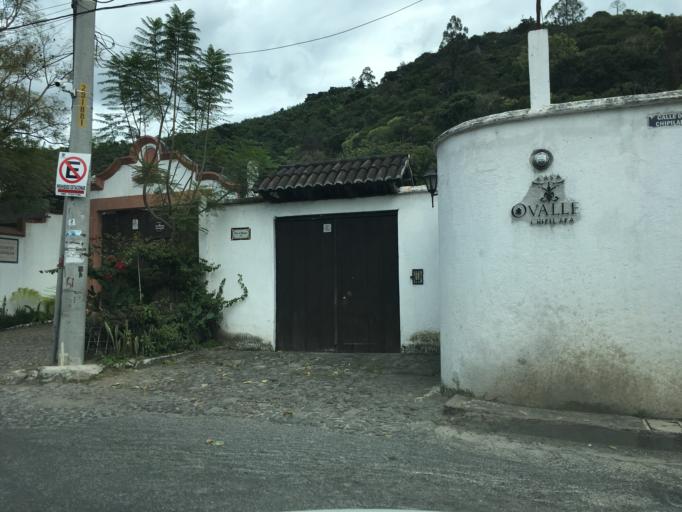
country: GT
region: Sacatepequez
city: Antigua Guatemala
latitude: 14.5545
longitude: -90.7271
